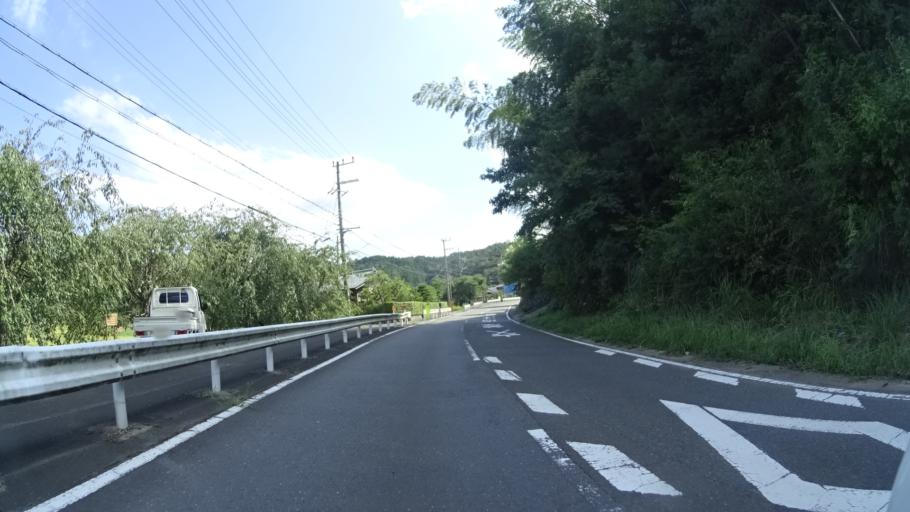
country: JP
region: Kyoto
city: Maizuru
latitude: 35.4434
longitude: 135.2957
